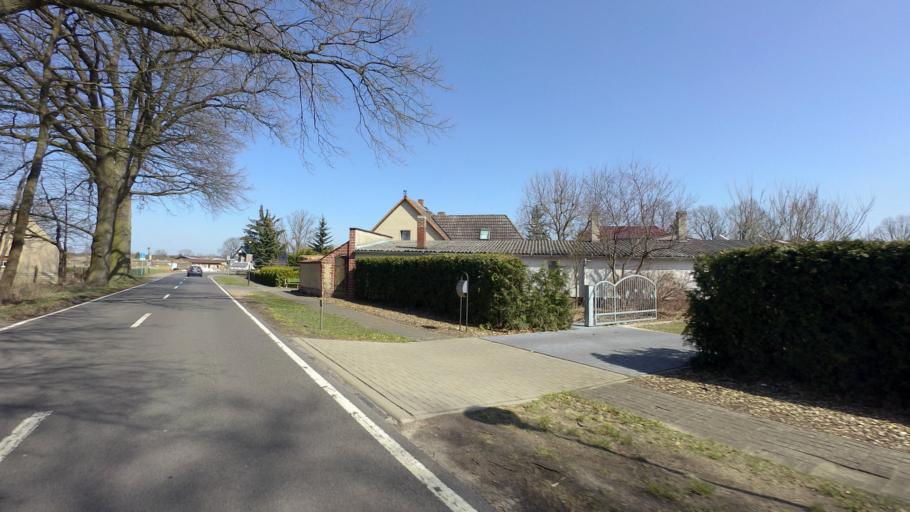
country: DE
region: Brandenburg
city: Lindow
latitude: 52.9303
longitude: 12.9669
